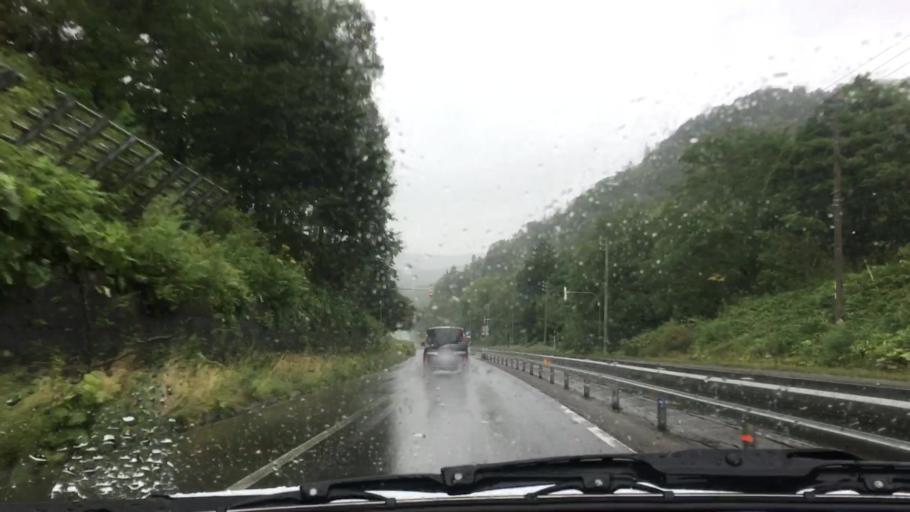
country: JP
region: Hokkaido
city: Otaru
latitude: 42.8470
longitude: 141.0532
